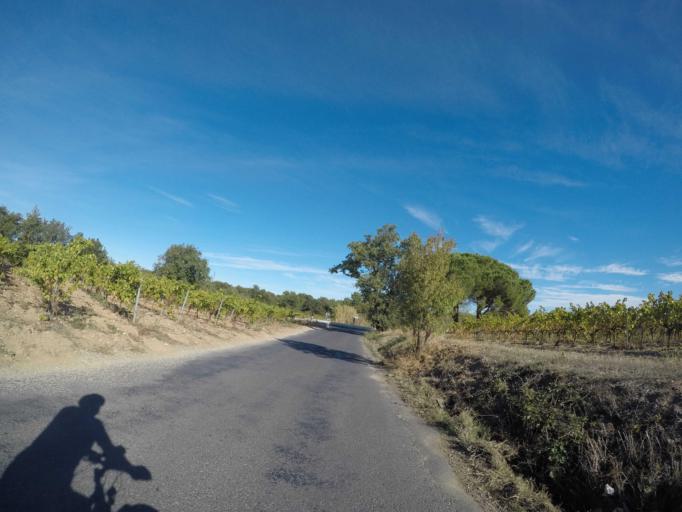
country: FR
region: Languedoc-Roussillon
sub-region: Departement des Pyrenees-Orientales
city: Trouillas
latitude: 42.5854
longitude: 2.8098
